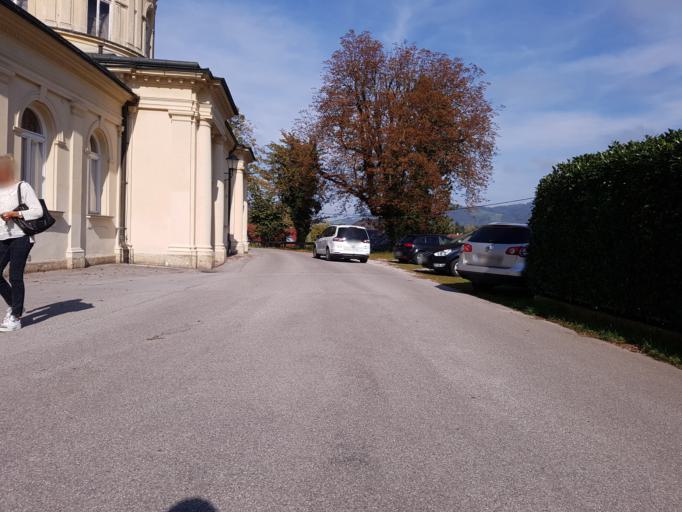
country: AT
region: Salzburg
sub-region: Salzburg Stadt
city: Salzburg
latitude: 47.7790
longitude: 13.0498
